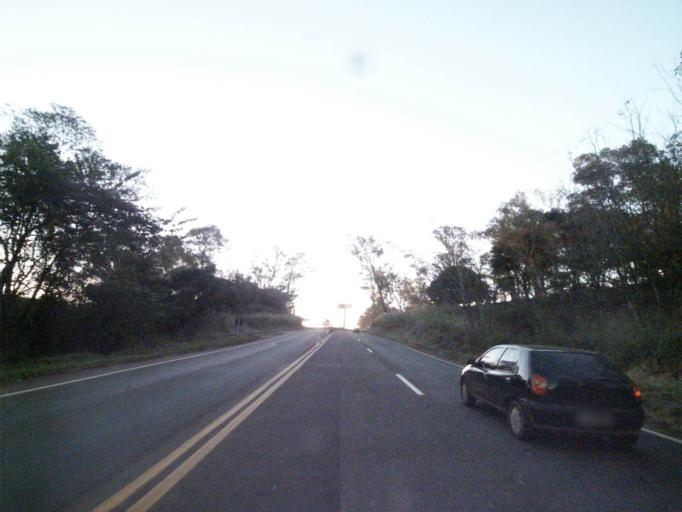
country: BR
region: Parana
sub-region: Londrina
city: Londrina
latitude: -23.4418
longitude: -51.1366
